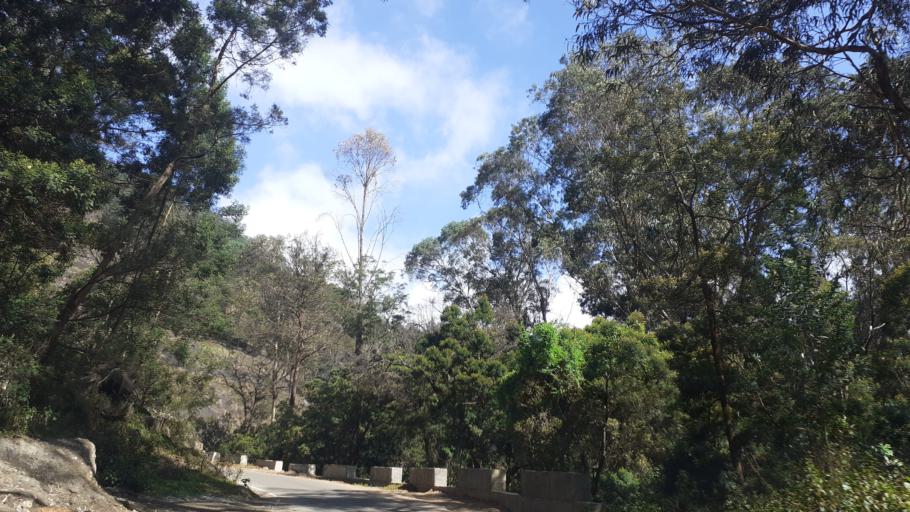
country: IN
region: Tamil Nadu
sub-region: Dindigul
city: Kodaikanal
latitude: 10.2246
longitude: 77.4221
